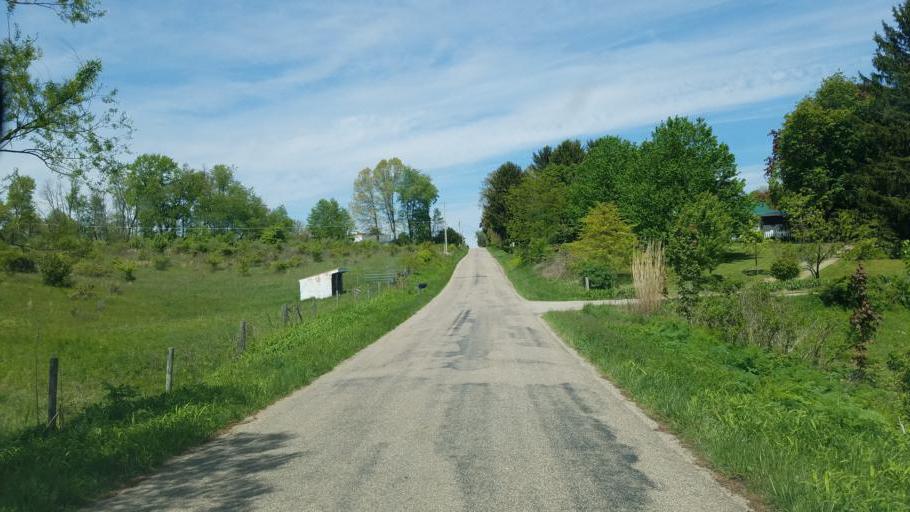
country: US
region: Ohio
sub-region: Knox County
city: Gambier
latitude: 40.3981
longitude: -82.4082
